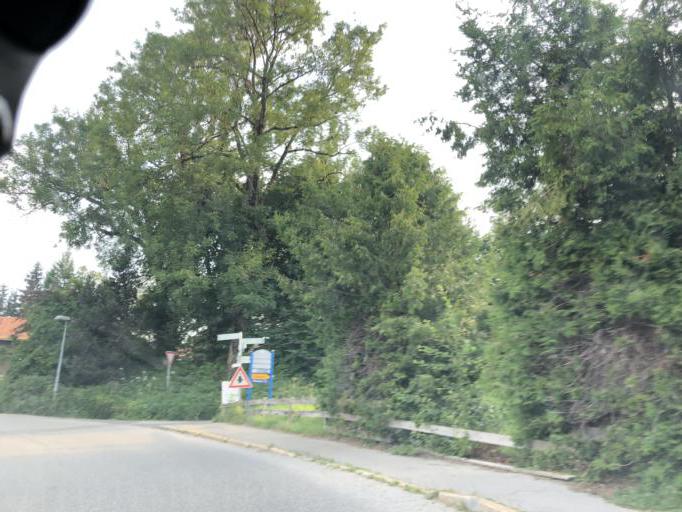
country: DE
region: Bavaria
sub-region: Swabia
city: Oy-Mittelberg
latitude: 47.6469
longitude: 10.4523
